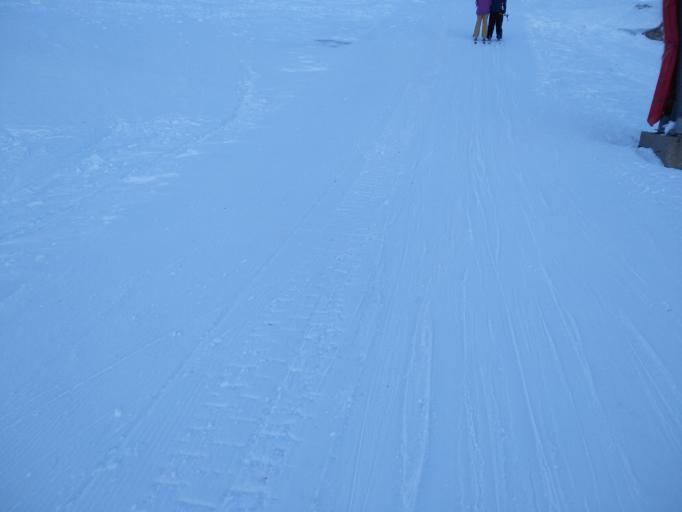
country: NO
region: Rogaland
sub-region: Sauda
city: Sauda
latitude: 59.6152
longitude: 6.2271
